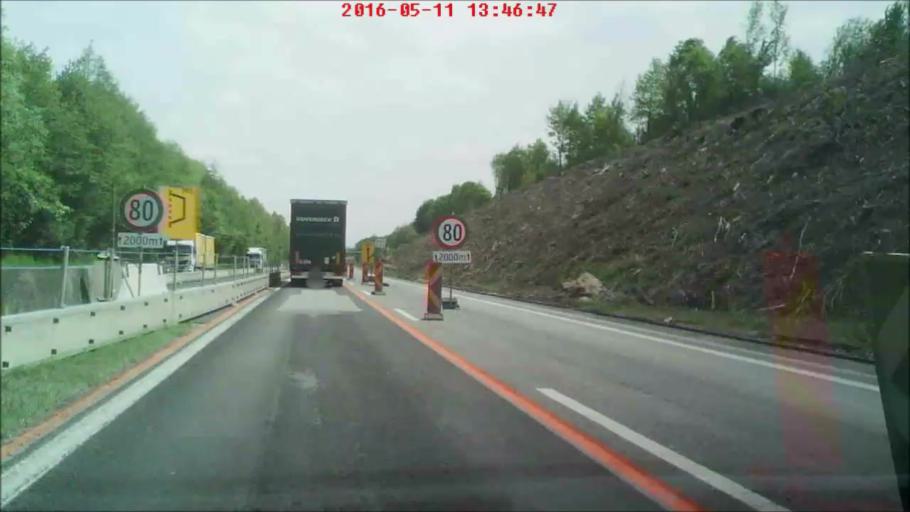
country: AT
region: Upper Austria
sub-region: Politischer Bezirk Vocklabruck
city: Wolfsegg am Hausruck
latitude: 48.2065
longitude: 13.6353
